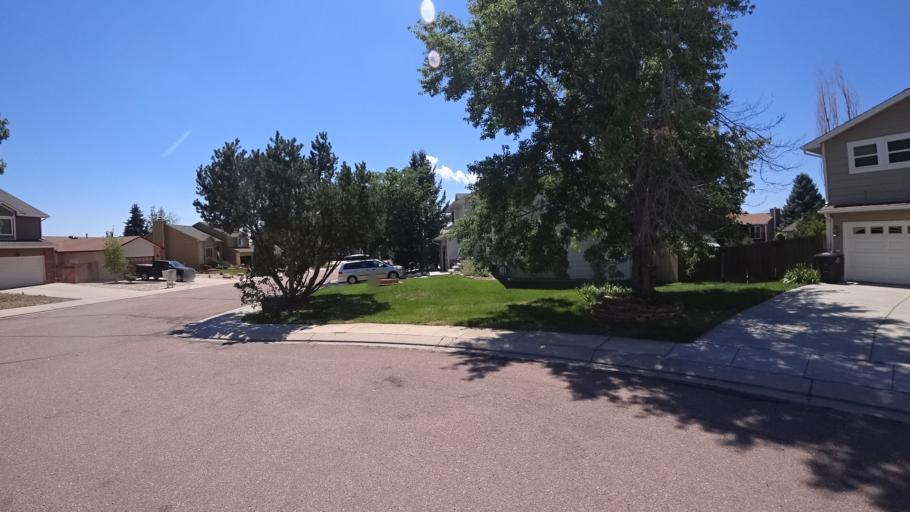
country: US
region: Colorado
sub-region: El Paso County
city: Black Forest
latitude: 38.9561
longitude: -104.7527
